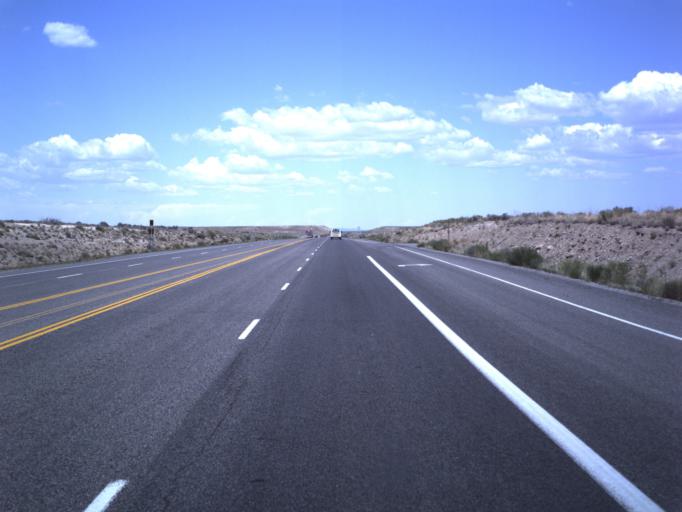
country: US
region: Utah
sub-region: Emery County
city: Huntington
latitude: 39.3630
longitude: -110.9239
